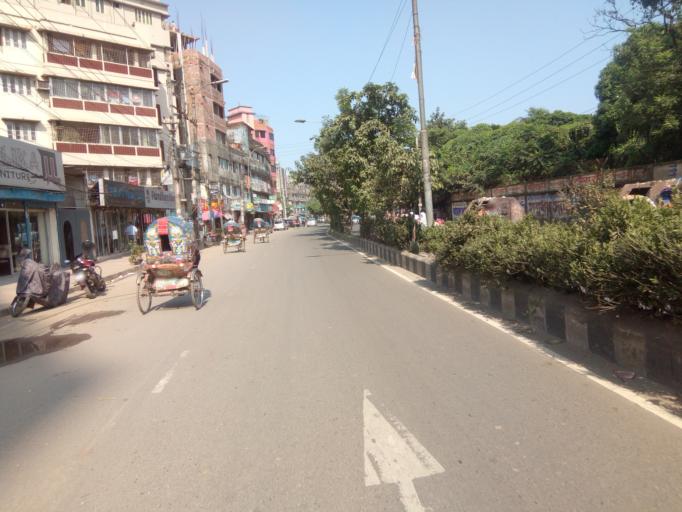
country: BD
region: Dhaka
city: Paltan
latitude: 23.7410
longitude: 90.4203
